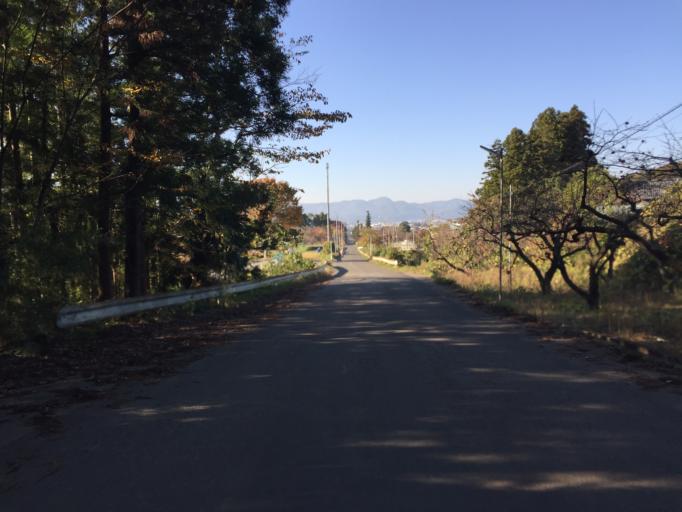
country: JP
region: Fukushima
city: Fukushima-shi
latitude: 37.7646
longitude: 140.5154
